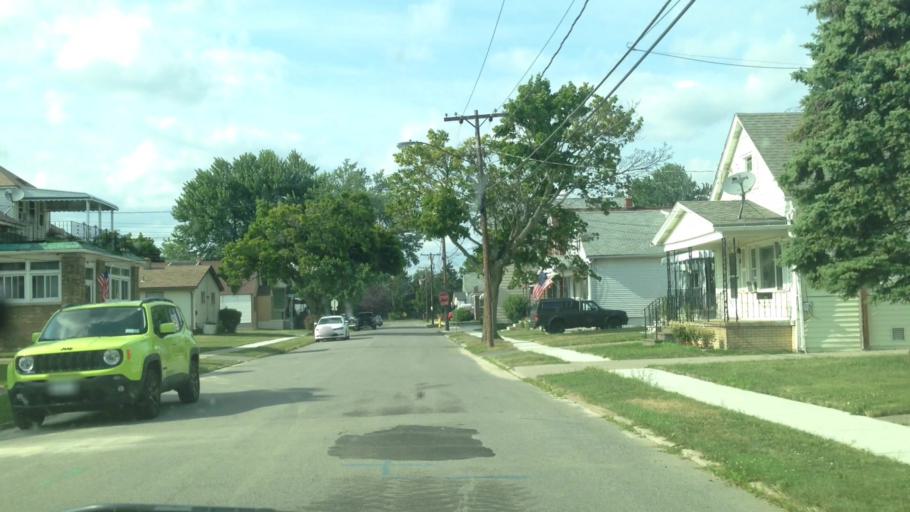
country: US
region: New York
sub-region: Erie County
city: Sloan
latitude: 42.8739
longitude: -78.7978
